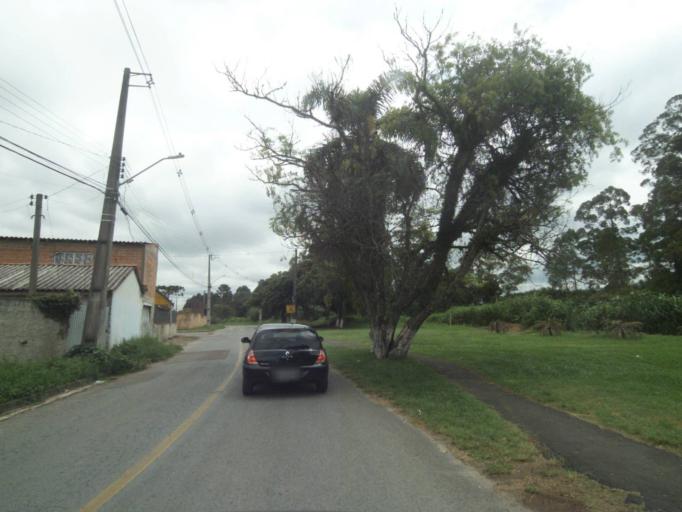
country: BR
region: Parana
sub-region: Pinhais
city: Pinhais
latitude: -25.4548
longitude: -49.1960
